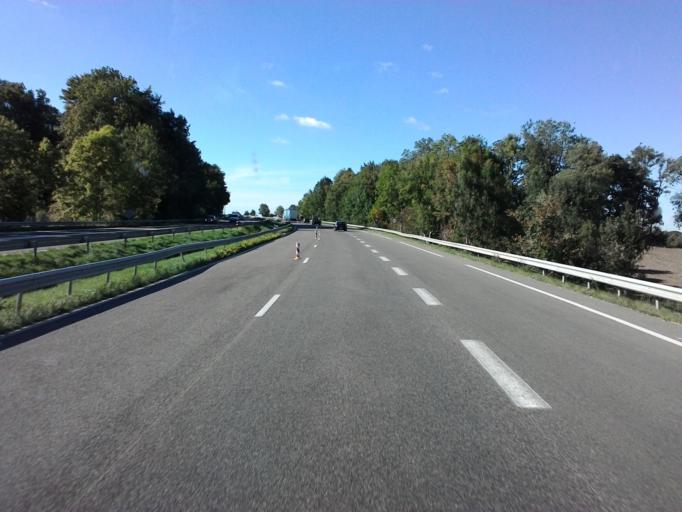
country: FR
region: Lorraine
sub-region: Departement de Meurthe-et-Moselle
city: Villers-la-Montagne
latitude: 49.4733
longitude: 5.8347
